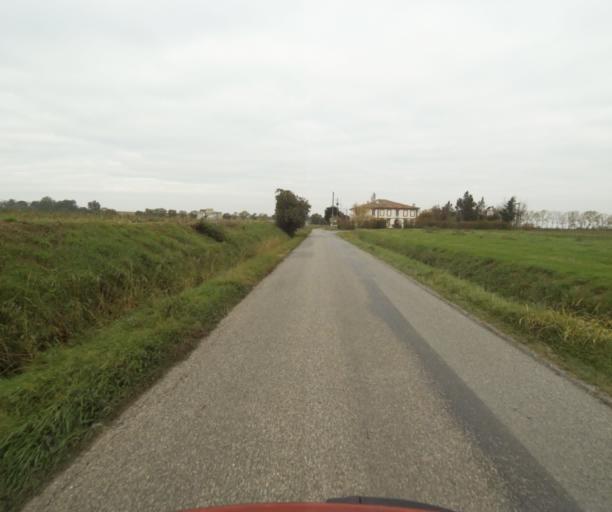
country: FR
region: Midi-Pyrenees
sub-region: Departement du Tarn-et-Garonne
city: Verdun-sur-Garonne
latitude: 43.8060
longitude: 1.2143
